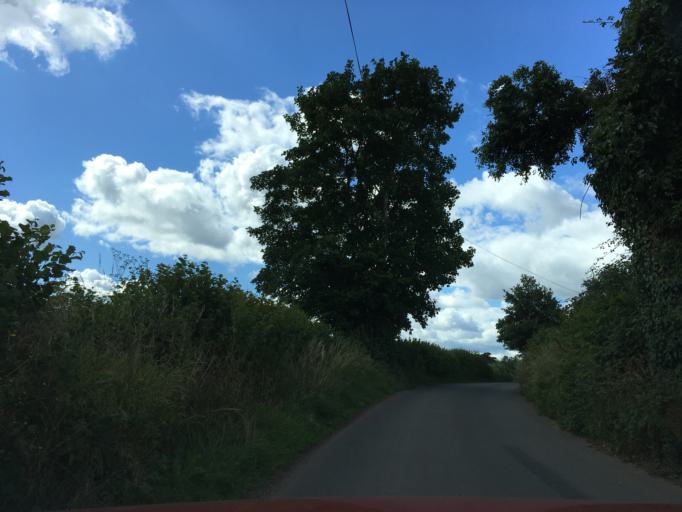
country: GB
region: England
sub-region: Gloucestershire
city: Mitcheldean
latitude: 51.8409
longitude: -2.4265
